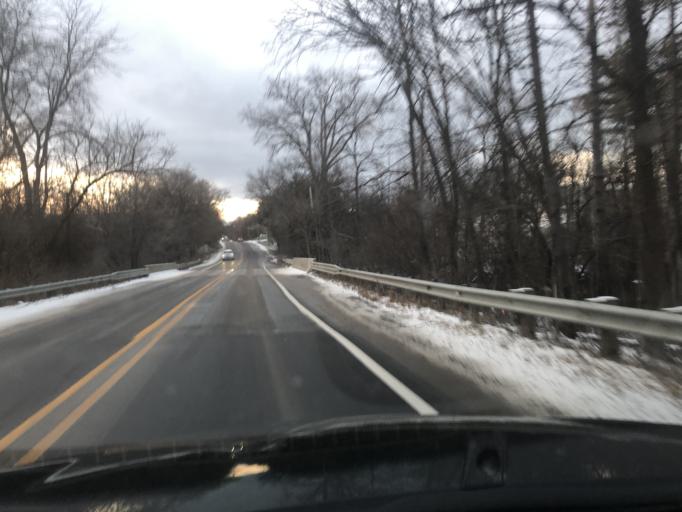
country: US
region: Michigan
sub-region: Oakland County
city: Milford
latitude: 42.5793
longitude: -83.6261
